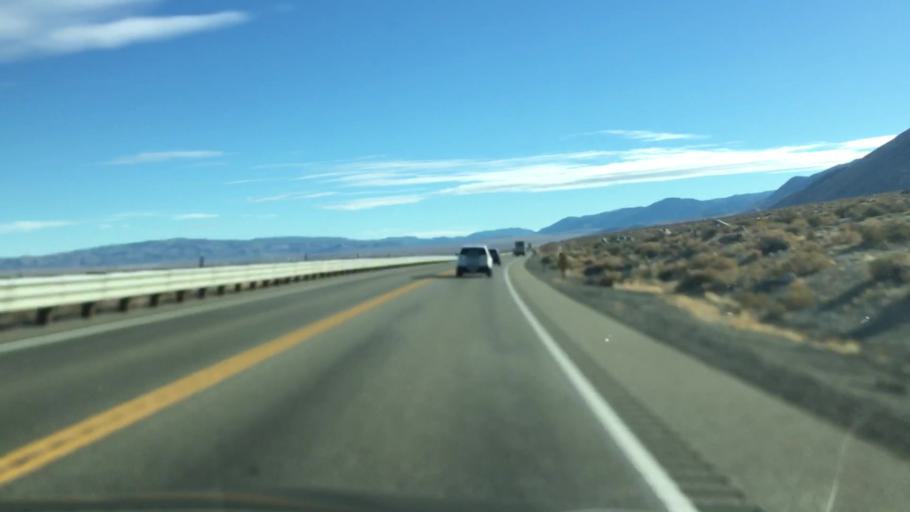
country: US
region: Nevada
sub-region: Mineral County
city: Hawthorne
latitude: 38.6060
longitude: -118.7123
